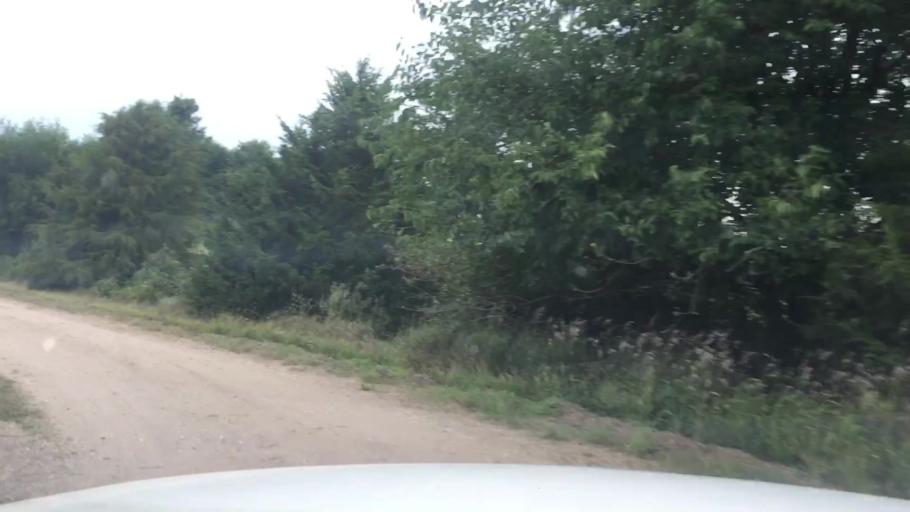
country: US
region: Iowa
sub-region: Story County
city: Huxley
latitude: 41.9176
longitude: -93.5726
